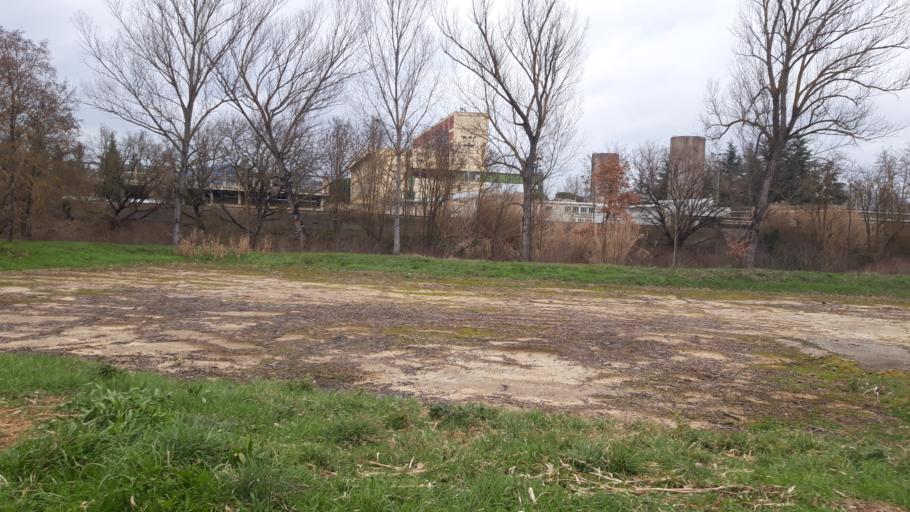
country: IT
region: Umbria
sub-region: Provincia di Perugia
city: Fontignano
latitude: 43.0021
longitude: 12.1821
